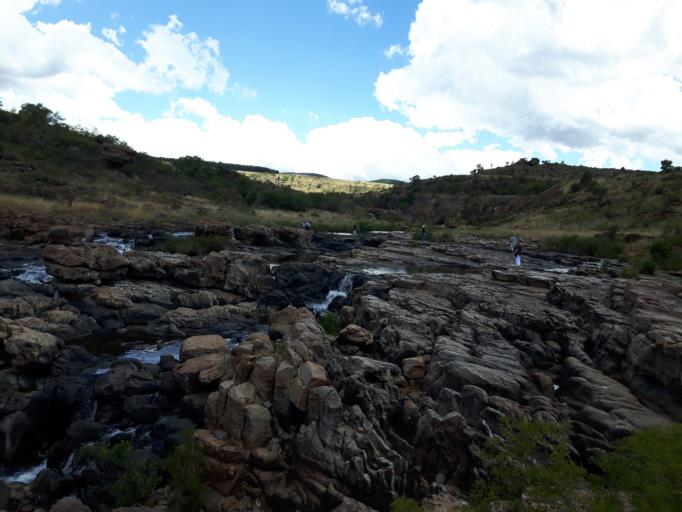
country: ZA
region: Mpumalanga
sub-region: Ehlanzeni District
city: Graksop
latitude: -24.6747
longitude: 30.8109
